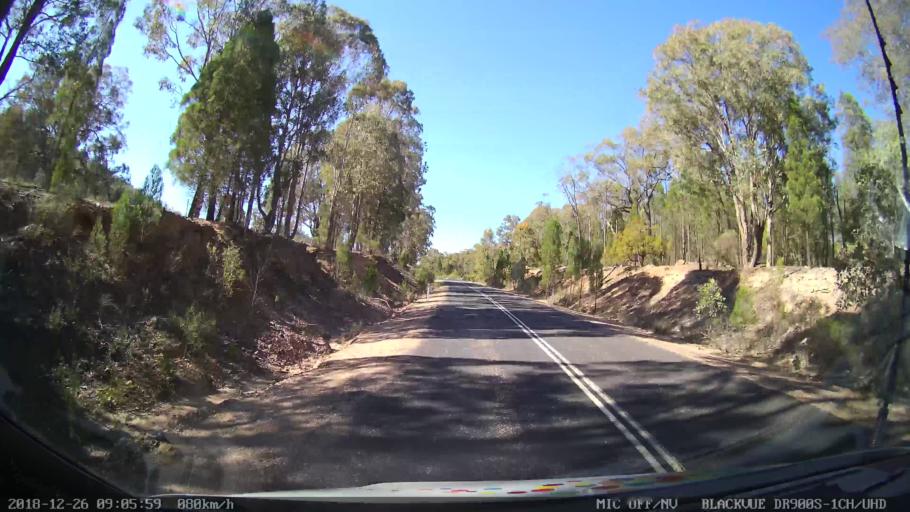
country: AU
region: New South Wales
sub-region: Mid-Western Regional
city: Kandos
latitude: -32.6888
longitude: 150.0047
